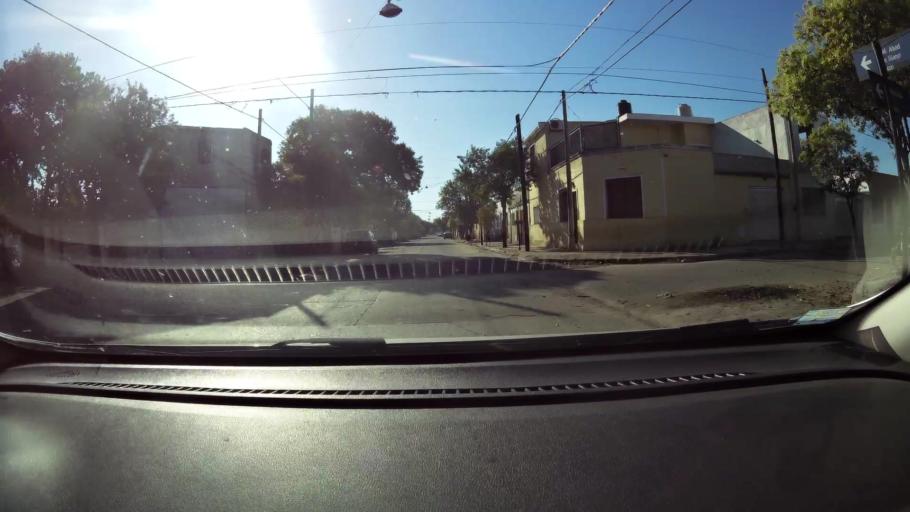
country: AR
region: Cordoba
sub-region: Departamento de Capital
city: Cordoba
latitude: -31.3856
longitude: -64.1726
